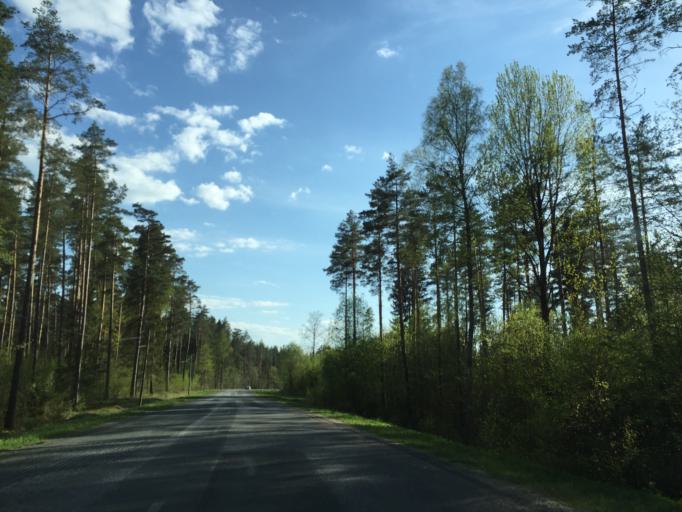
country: LV
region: Sigulda
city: Sigulda
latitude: 57.2455
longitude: 24.8661
